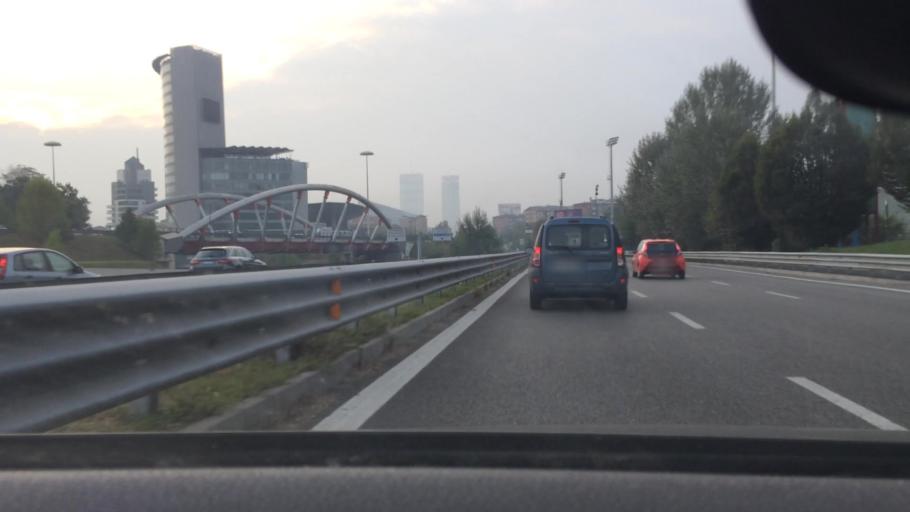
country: IT
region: Lombardy
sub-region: Citta metropolitana di Milano
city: Novate Milanese
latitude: 45.4919
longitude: 9.1369
